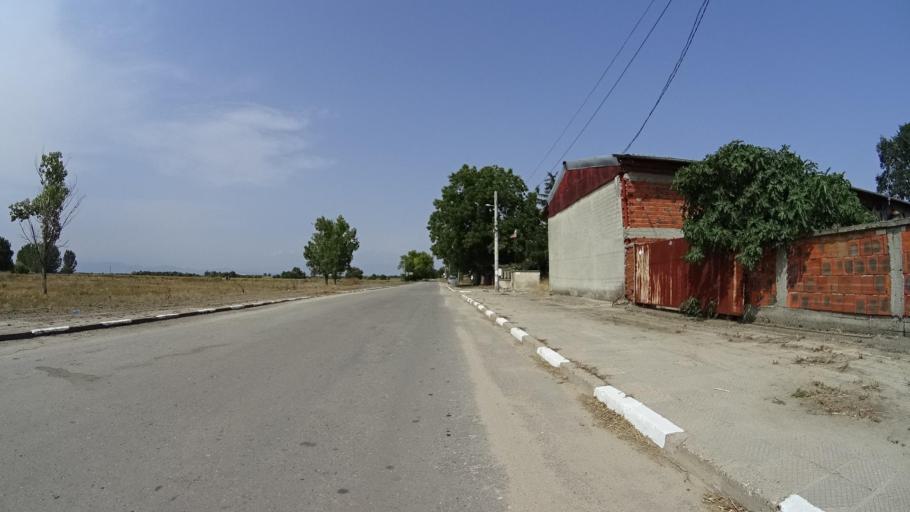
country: BG
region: Plovdiv
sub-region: Obshtina Plovdiv
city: Plovdiv
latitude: 42.2461
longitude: 24.7958
